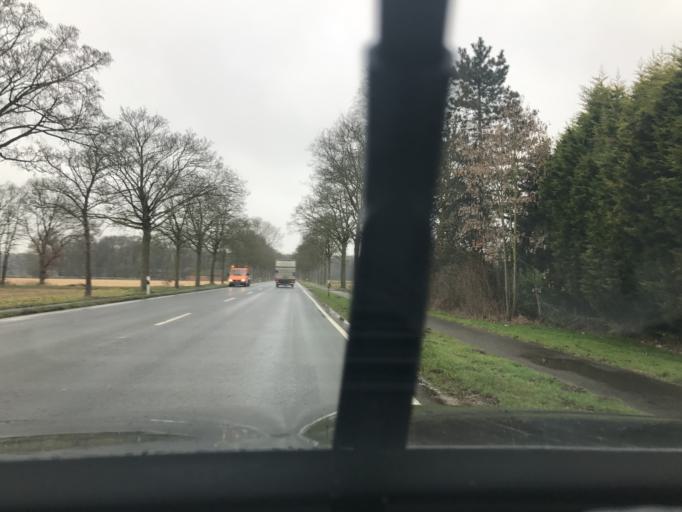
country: DE
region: North Rhine-Westphalia
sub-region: Regierungsbezirk Dusseldorf
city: Wachtendonk
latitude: 51.4229
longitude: 6.3656
